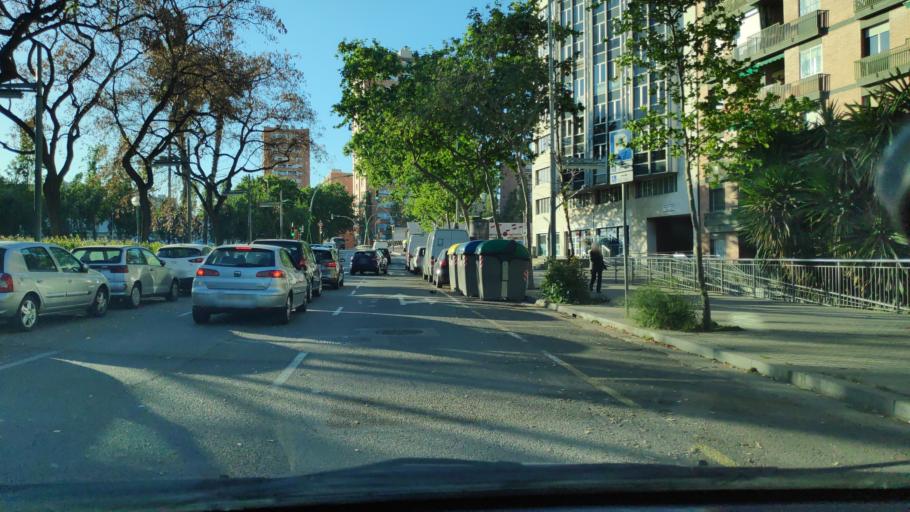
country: ES
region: Catalonia
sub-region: Provincia de Barcelona
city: Sant Marti
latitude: 41.4190
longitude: 2.2096
